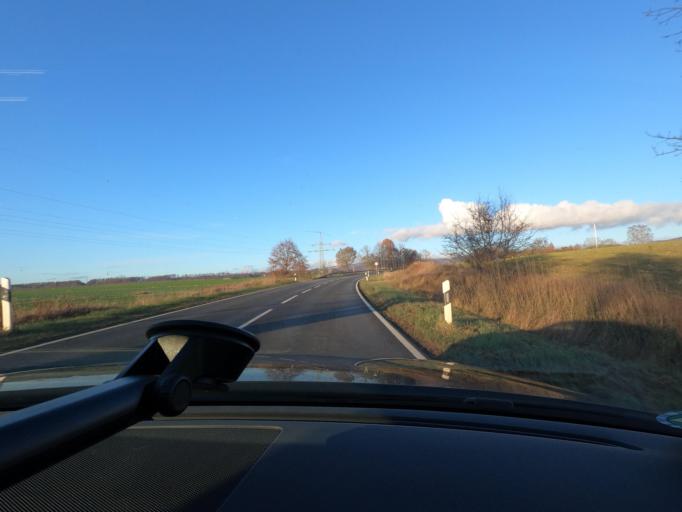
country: DE
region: Lower Saxony
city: Herzberg am Harz
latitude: 51.6362
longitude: 10.3298
